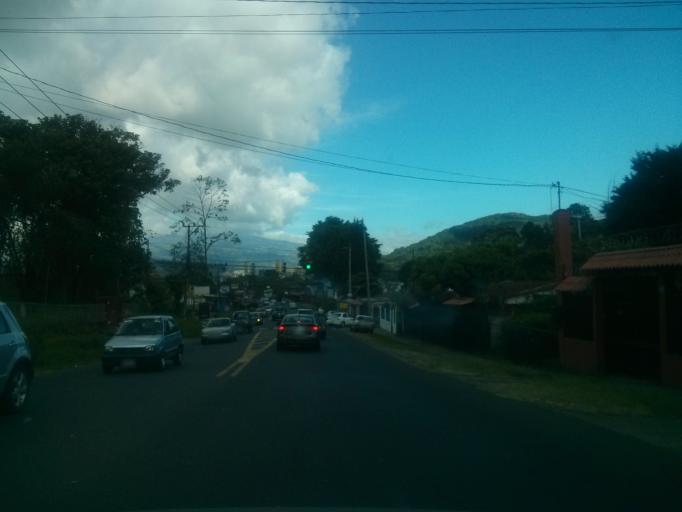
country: CR
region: San Jose
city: San Rafael Arriba
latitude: 9.8810
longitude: -84.0724
